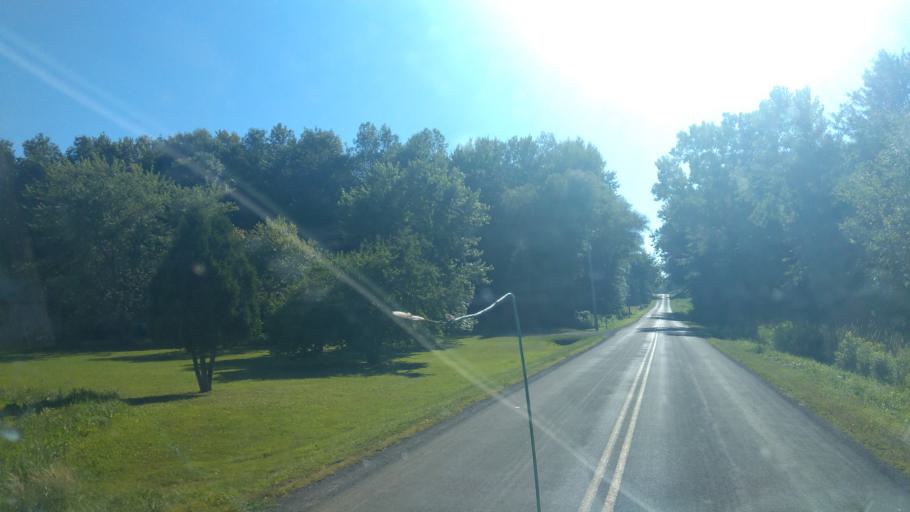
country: US
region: New York
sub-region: Seneca County
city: Waterloo
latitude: 42.9894
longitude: -76.8576
